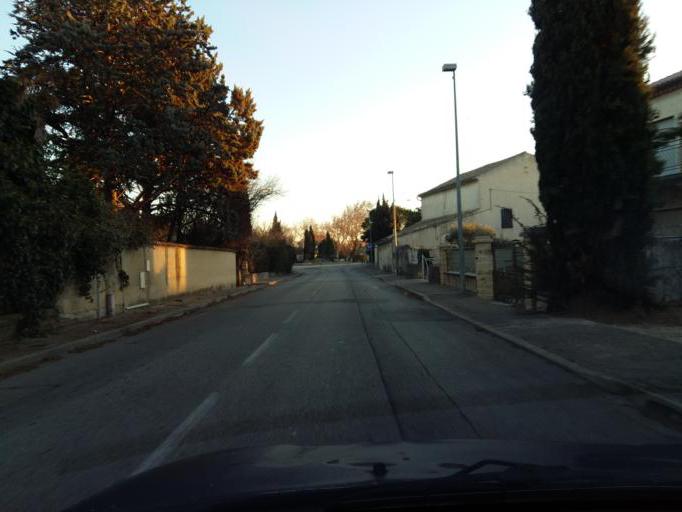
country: FR
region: Provence-Alpes-Cote d'Azur
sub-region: Departement du Vaucluse
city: Sainte-Cecile-les-Vignes
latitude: 44.2480
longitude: 4.8867
